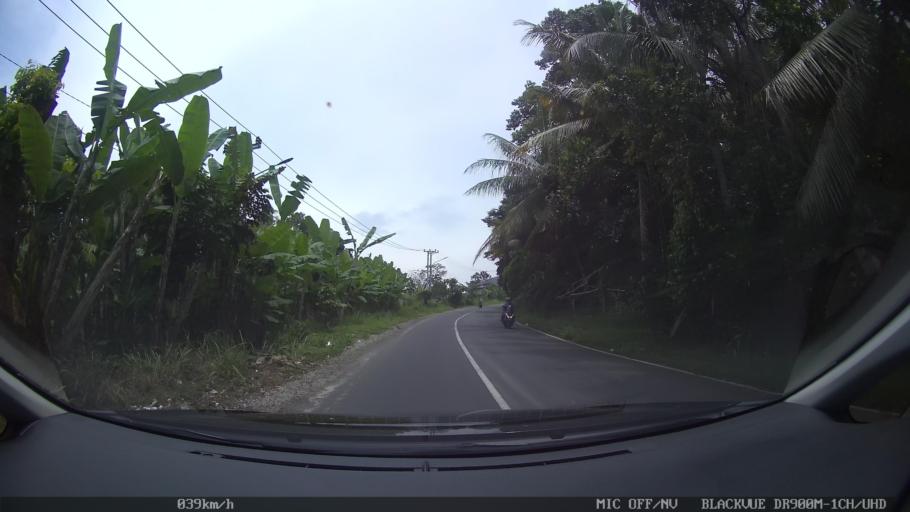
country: ID
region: Lampung
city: Bandarlampung
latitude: -5.4298
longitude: 105.2370
